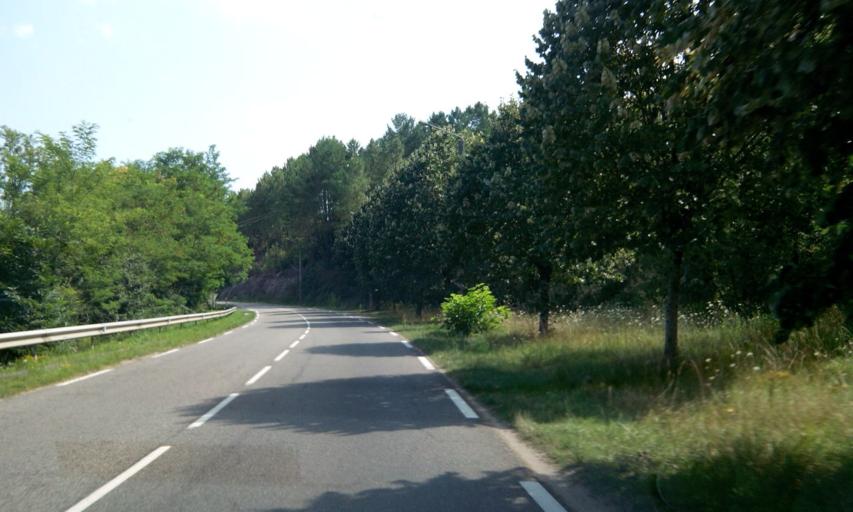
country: FR
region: Limousin
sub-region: Departement de la Correze
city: Brive-la-Gaillarde
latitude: 45.1391
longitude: 1.5492
